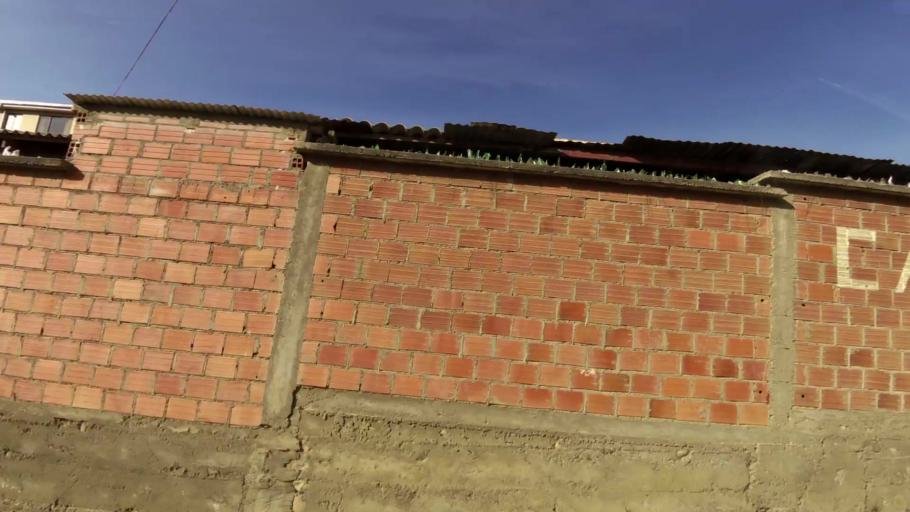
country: BO
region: La Paz
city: La Paz
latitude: -16.5033
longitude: -68.0819
